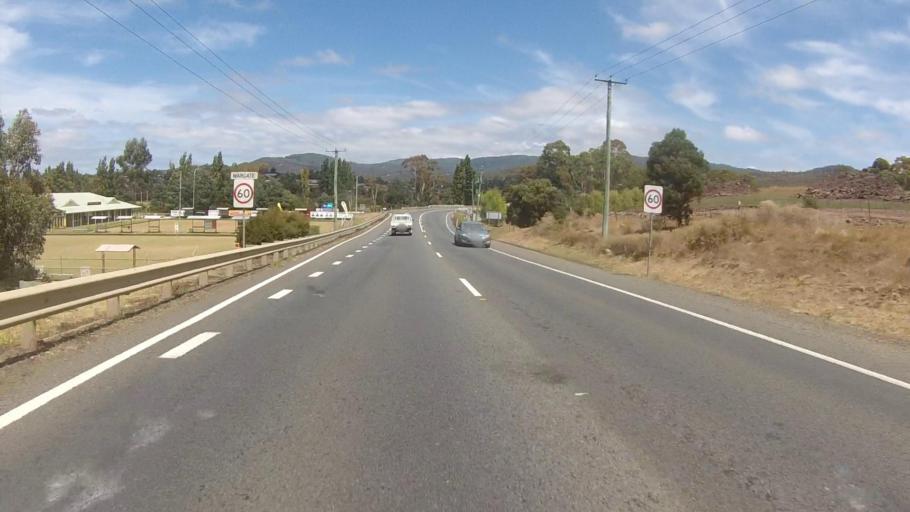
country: AU
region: Tasmania
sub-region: Kingborough
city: Margate
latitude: -43.0201
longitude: 147.2676
